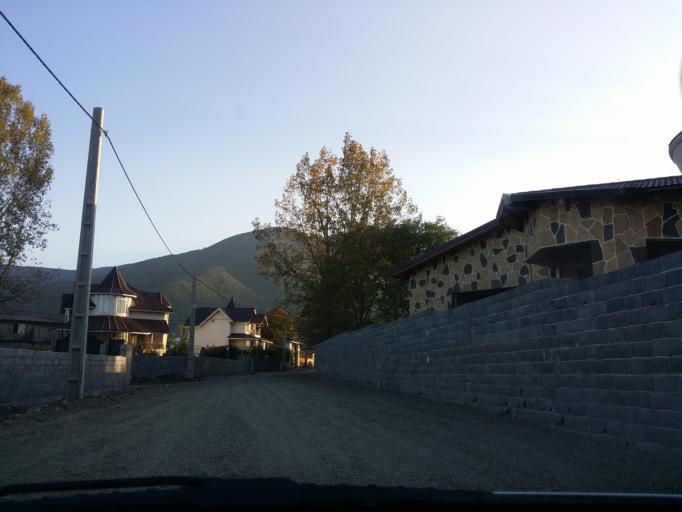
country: IR
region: Mazandaran
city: `Abbasabad
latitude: 36.5163
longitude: 51.1911
